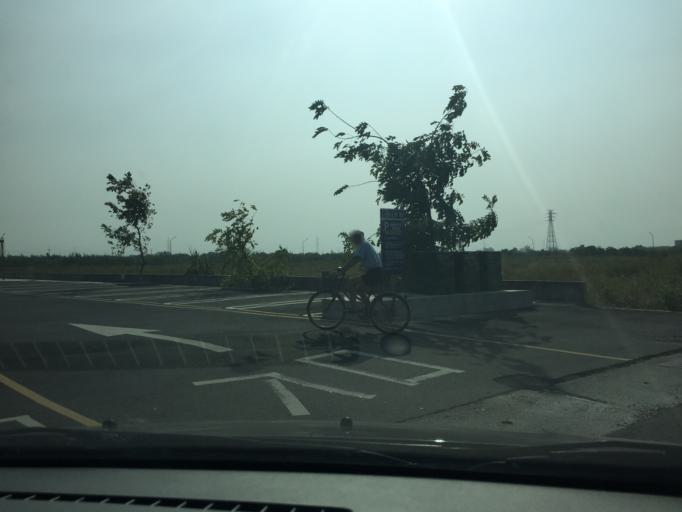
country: TW
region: Taiwan
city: Xinying
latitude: 23.1931
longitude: 120.3128
